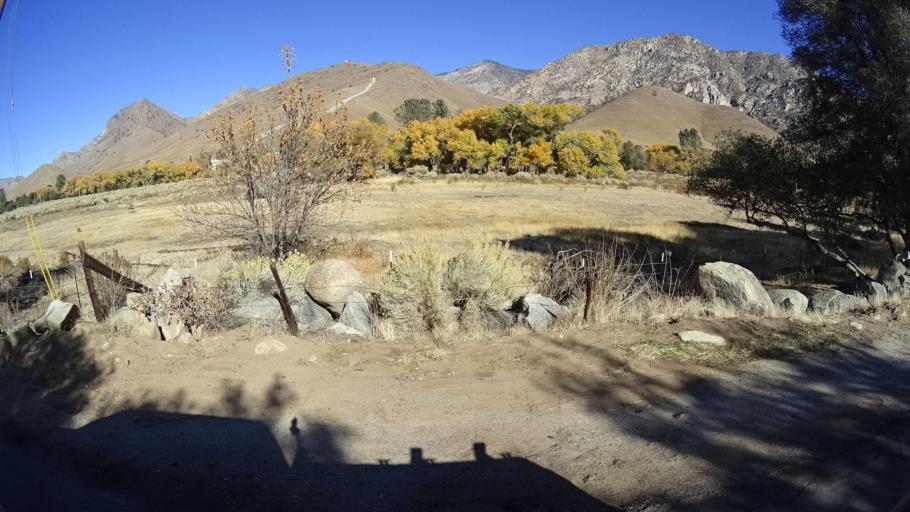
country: US
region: California
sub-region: Kern County
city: Kernville
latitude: 35.7705
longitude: -118.4374
